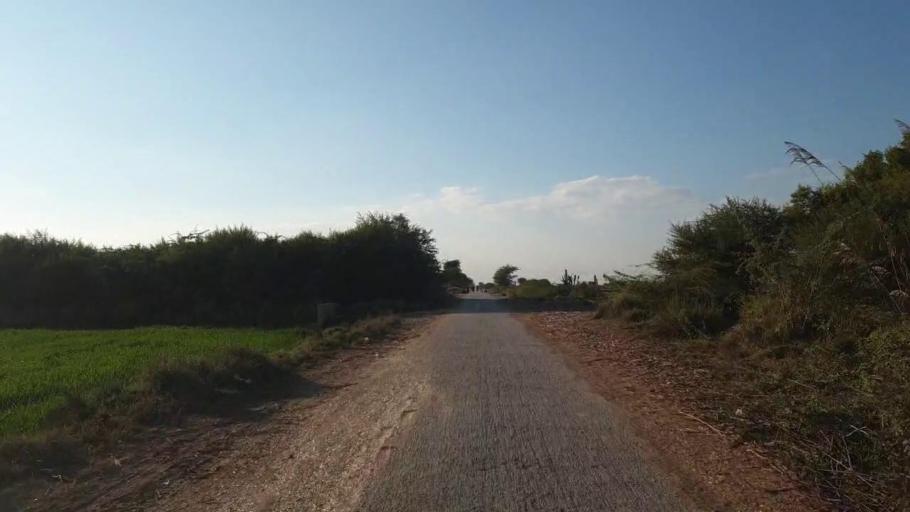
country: PK
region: Sindh
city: Shahpur Chakar
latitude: 26.1405
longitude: 68.5494
